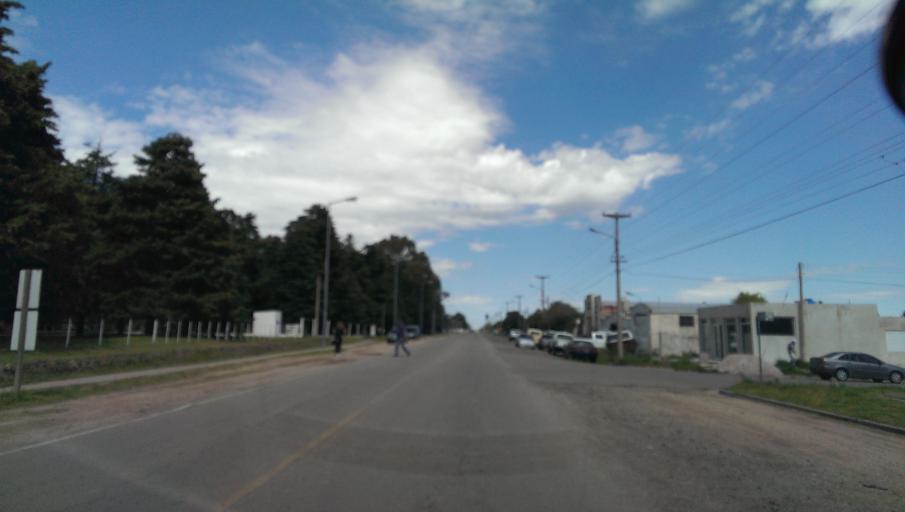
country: AR
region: Buenos Aires
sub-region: Partido de Tornquist
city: Tornquist
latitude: -38.0959
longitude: -62.2184
